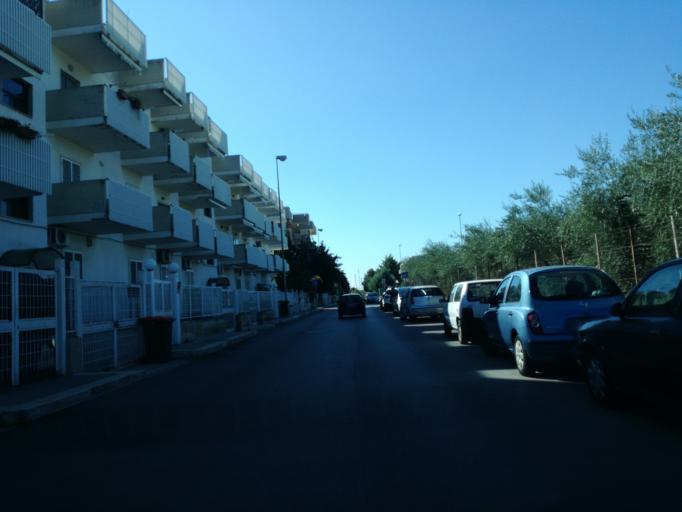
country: IT
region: Apulia
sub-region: Provincia di Bari
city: Capurso
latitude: 41.0495
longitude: 16.9154
